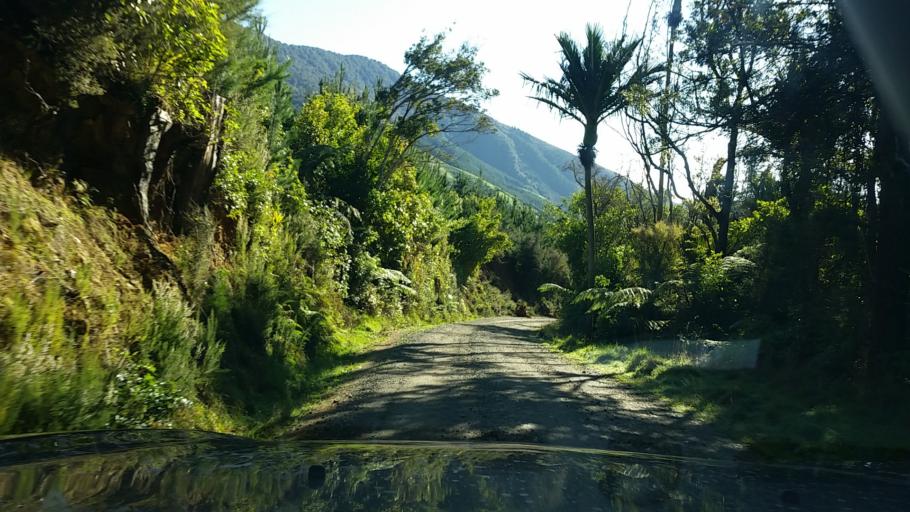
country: NZ
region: Marlborough
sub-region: Marlborough District
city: Picton
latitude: -41.1334
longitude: 174.0404
